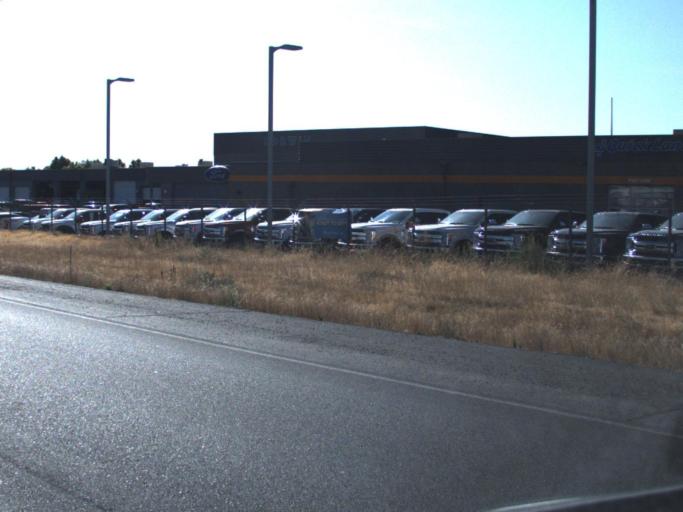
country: US
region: Washington
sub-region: Benton County
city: Kennewick
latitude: 46.2388
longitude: -119.1300
